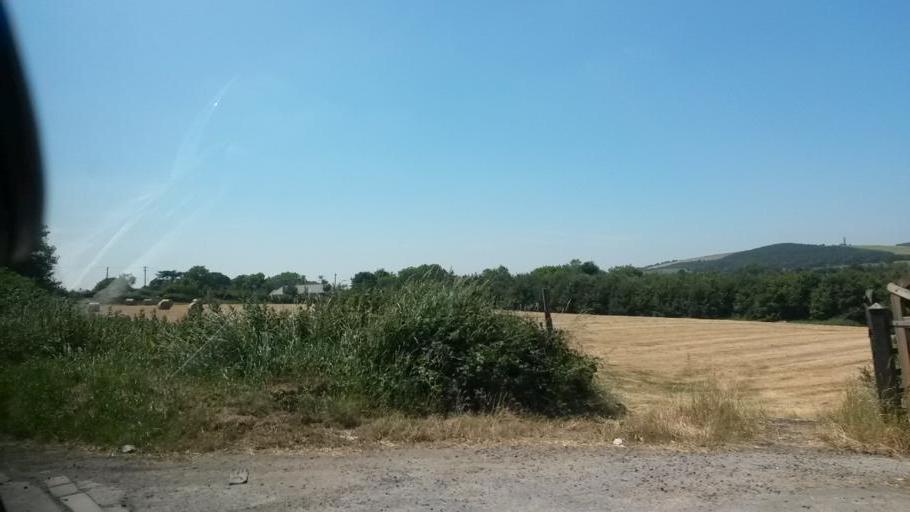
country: IE
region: Leinster
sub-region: An Mhi
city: Stamullin
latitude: 53.5888
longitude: -6.2823
